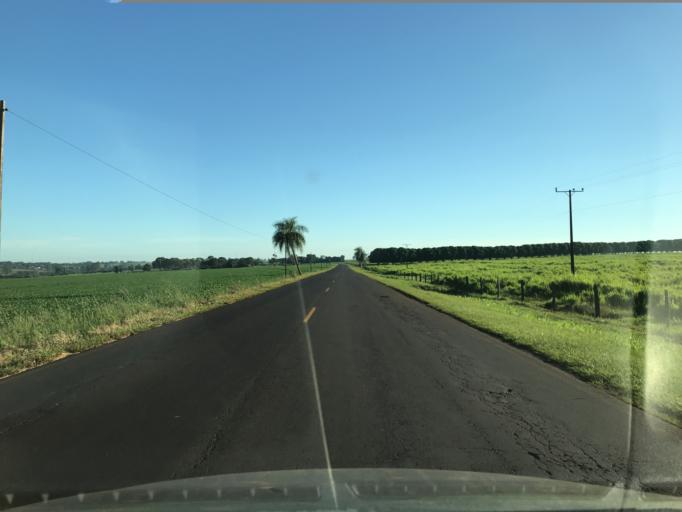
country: BR
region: Parana
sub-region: Ipora
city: Ipora
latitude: -24.1055
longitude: -53.8410
